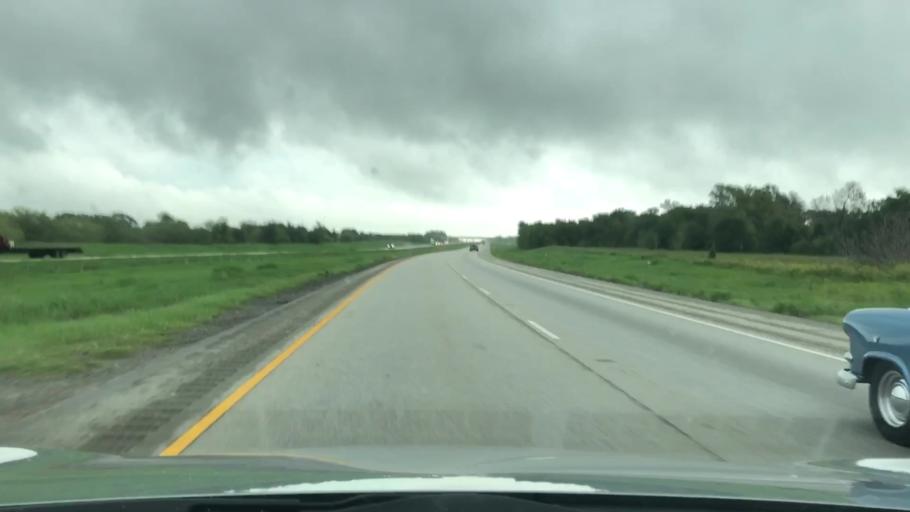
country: US
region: Texas
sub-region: Fayette County
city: Flatonia
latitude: 29.6964
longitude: -97.1394
